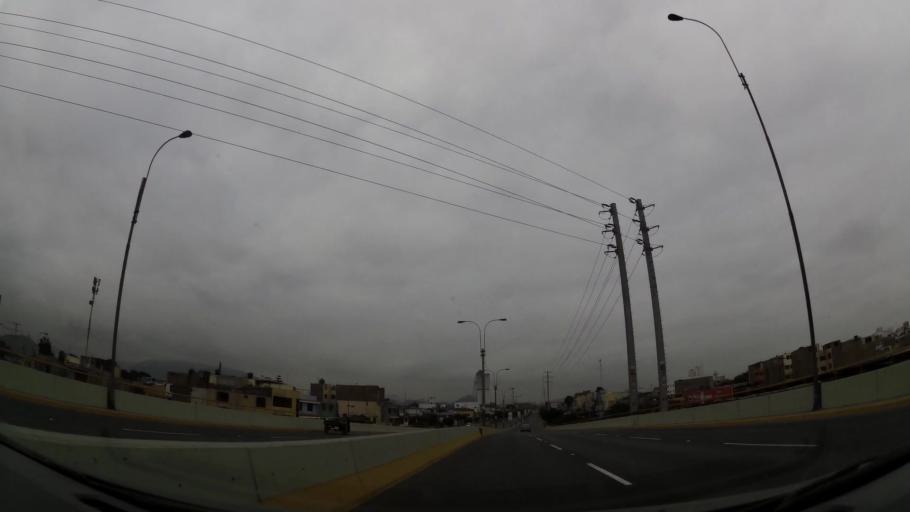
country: PE
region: Callao
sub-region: Callao
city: Callao
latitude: -12.0501
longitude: -77.0778
